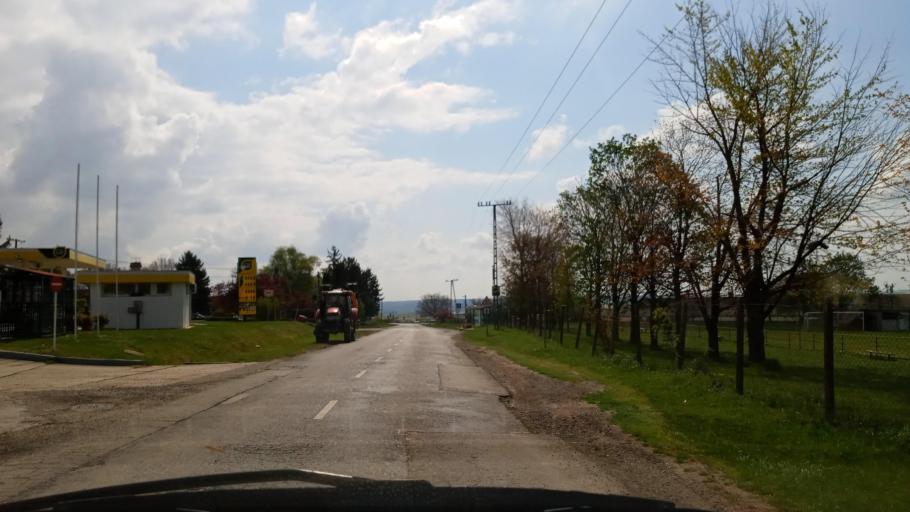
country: HU
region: Baranya
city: Pecsvarad
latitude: 46.1083
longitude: 18.5184
